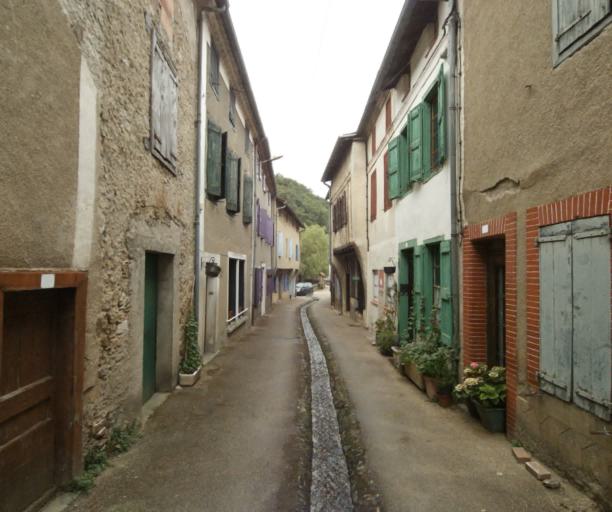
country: FR
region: Midi-Pyrenees
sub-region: Departement du Tarn
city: Soreze
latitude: 43.4382
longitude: 2.0675
